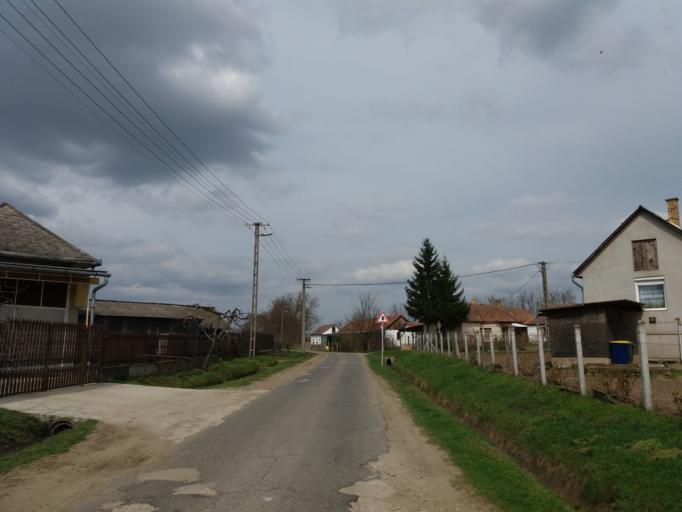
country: HU
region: Szabolcs-Szatmar-Bereg
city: Petnehaza
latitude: 48.0609
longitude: 22.0450
